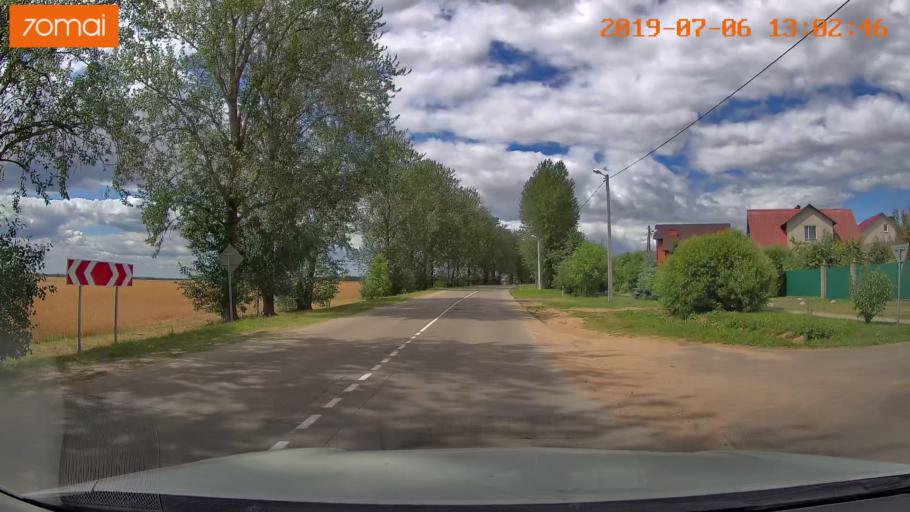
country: BY
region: Minsk
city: Dzyarzhynsk
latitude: 53.6872
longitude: 27.1119
